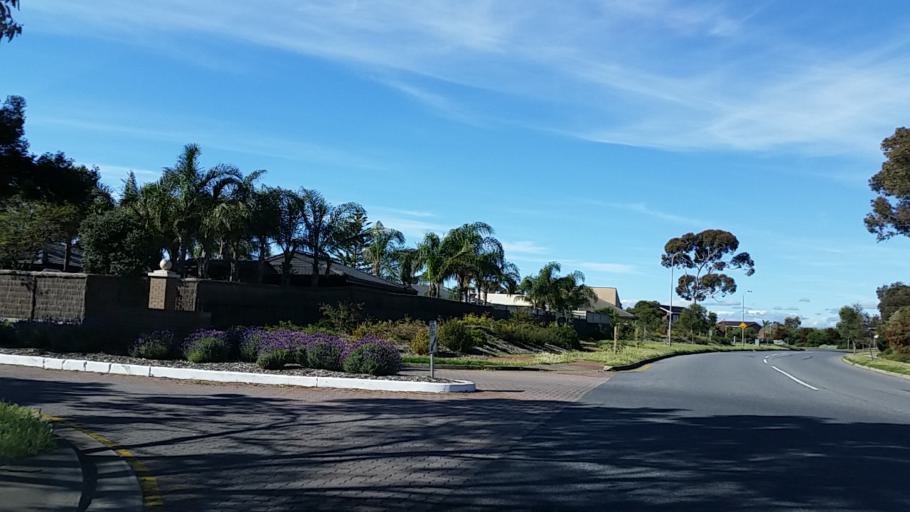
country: AU
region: South Australia
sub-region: Charles Sturt
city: West Lakes Shore
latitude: -34.8694
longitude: 138.4895
